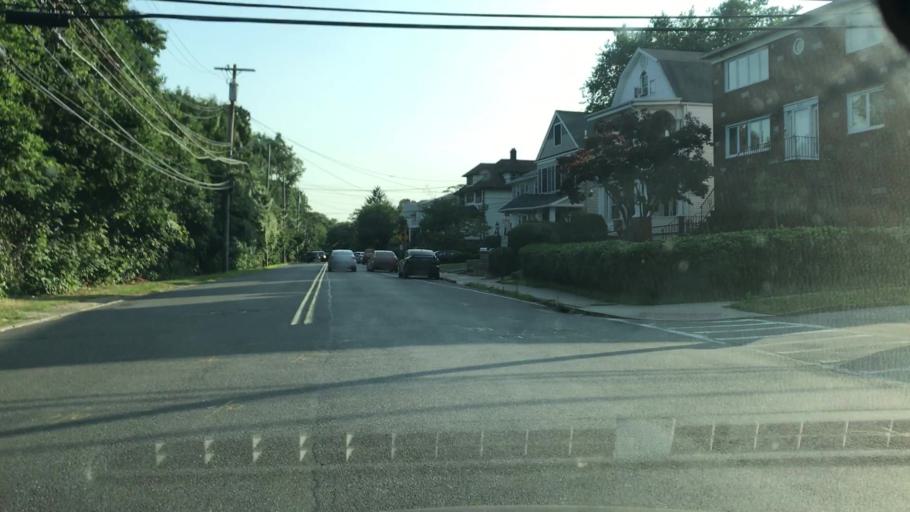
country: US
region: New York
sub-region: Westchester County
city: Yonkers
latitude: 40.9443
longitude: -73.8669
